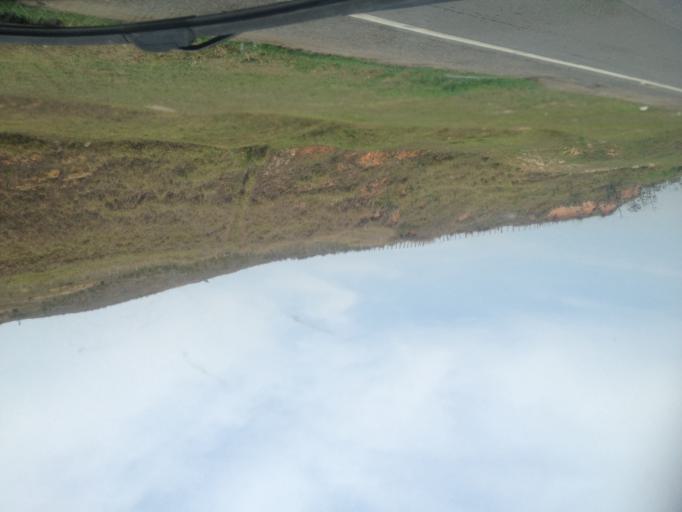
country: BR
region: Rio de Janeiro
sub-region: Porto Real
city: Porto Real
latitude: -22.4494
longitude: -44.3222
